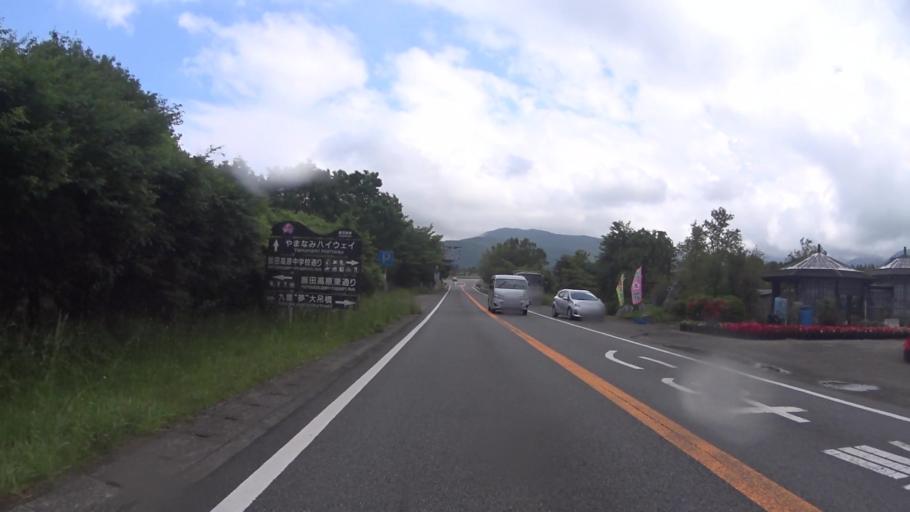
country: JP
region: Oita
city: Tsukawaki
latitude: 33.1593
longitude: 131.2401
